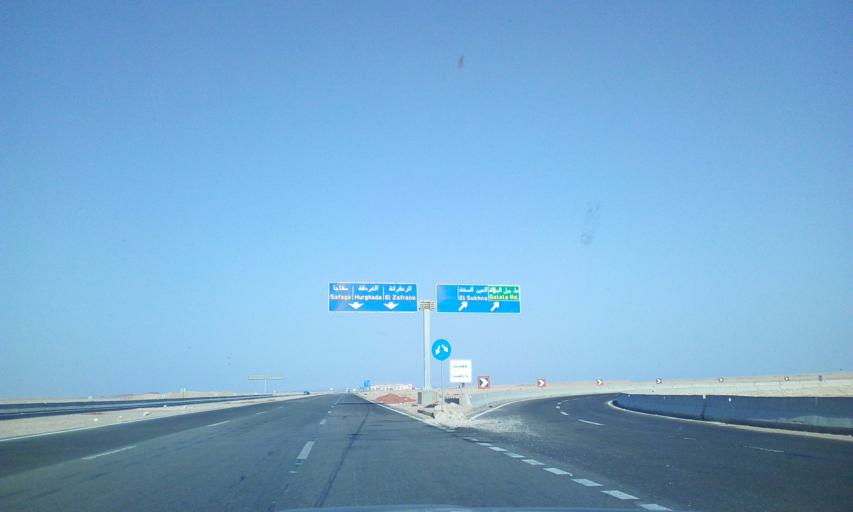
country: EG
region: As Suways
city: Ain Sukhna
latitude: 29.1093
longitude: 32.5358
